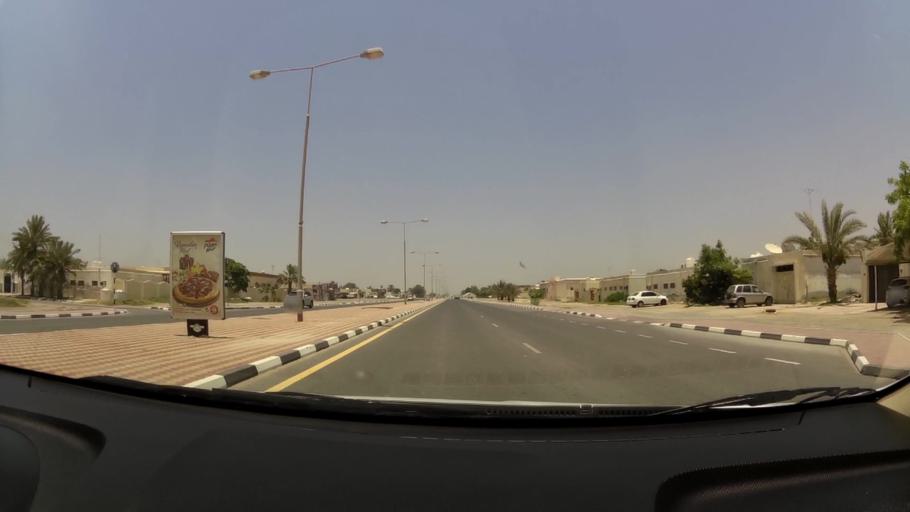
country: AE
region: Umm al Qaywayn
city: Umm al Qaywayn
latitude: 25.5577
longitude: 55.5570
